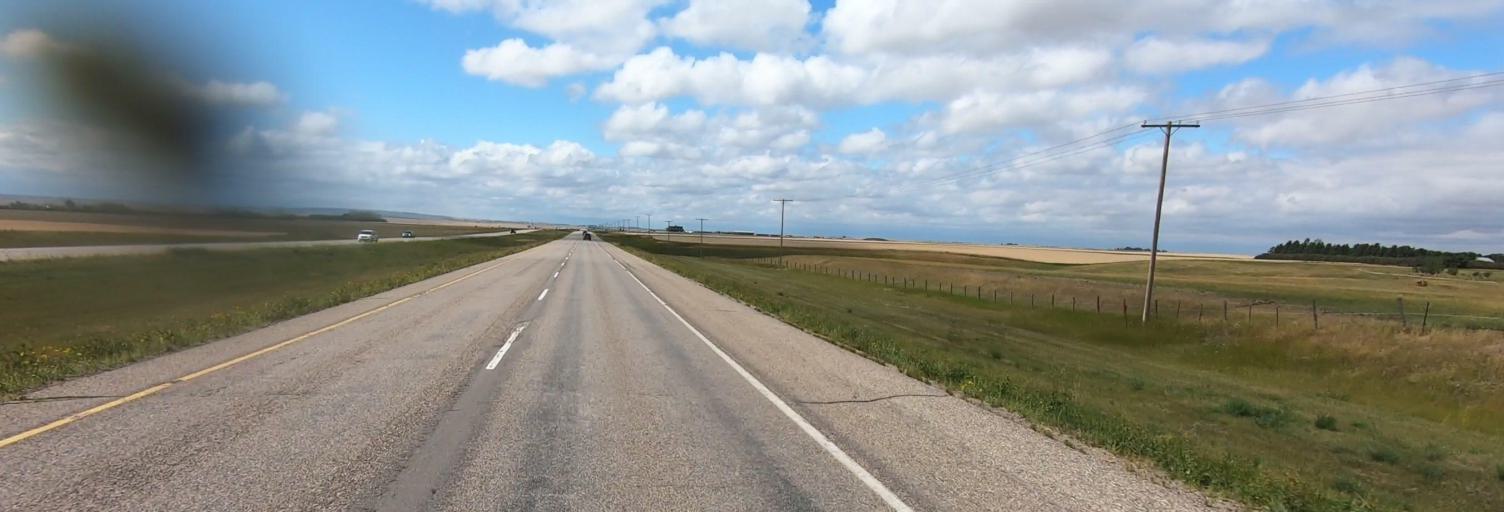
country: CA
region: Saskatchewan
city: Moose Jaw
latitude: 50.4261
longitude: -105.7010
